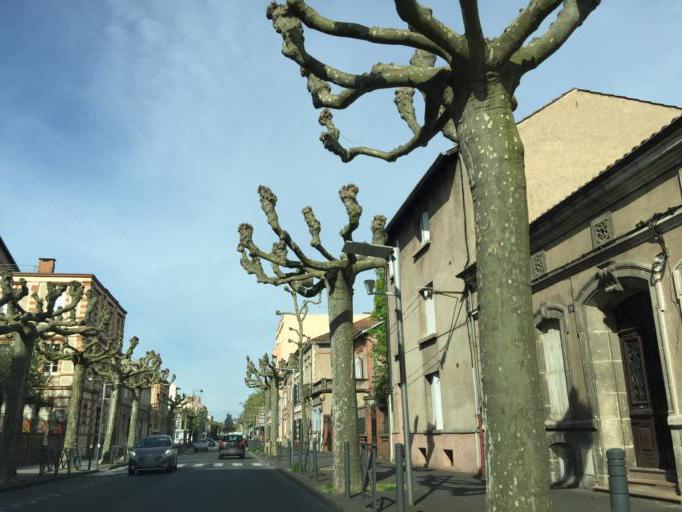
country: FR
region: Midi-Pyrenees
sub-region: Departement du Tarn
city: Albi
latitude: 43.9227
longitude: 2.1440
